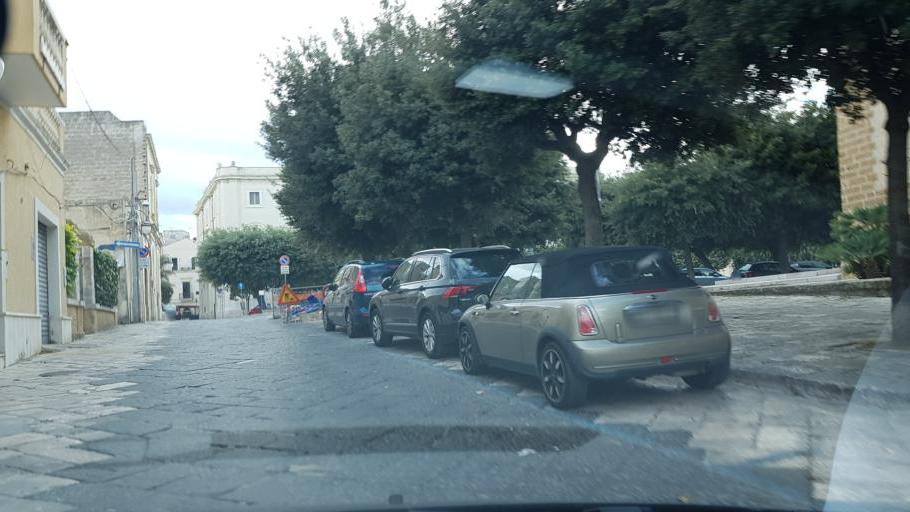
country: IT
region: Apulia
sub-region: Provincia di Brindisi
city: Brindisi
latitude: 40.6407
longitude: 17.9442
